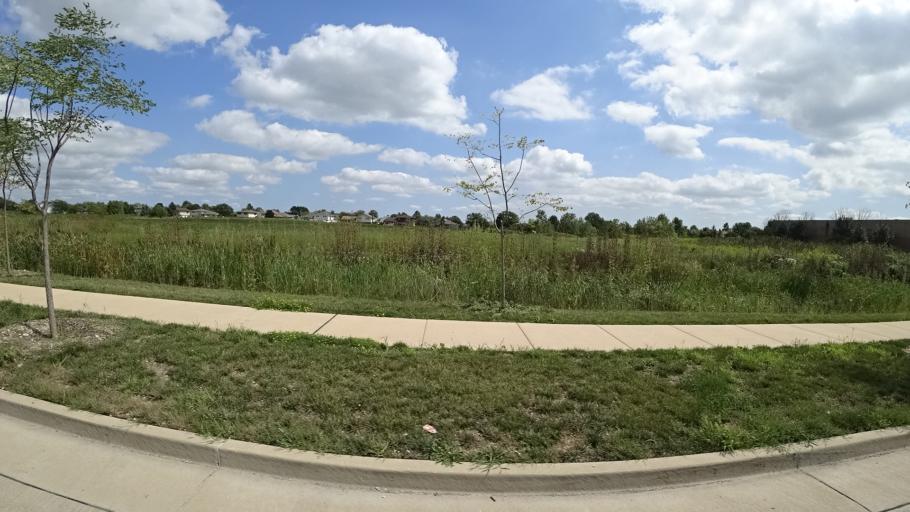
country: US
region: Illinois
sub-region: Cook County
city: Orland Hills
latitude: 41.5673
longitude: -87.8513
